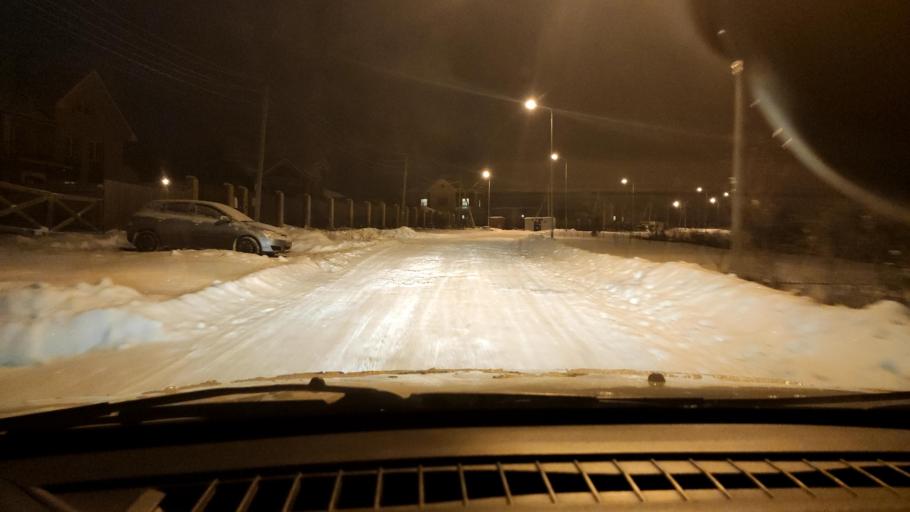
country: RU
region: Perm
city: Perm
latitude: 58.0271
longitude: 56.3452
